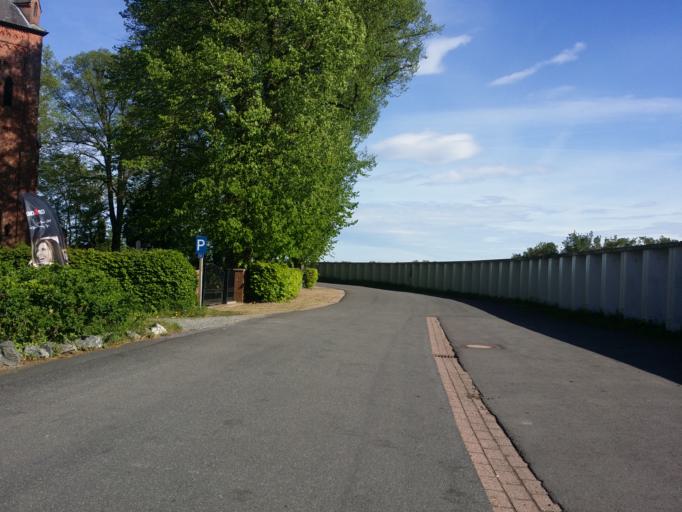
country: DE
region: Lower Saxony
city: Lemwerder
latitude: 53.1286
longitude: 8.6532
